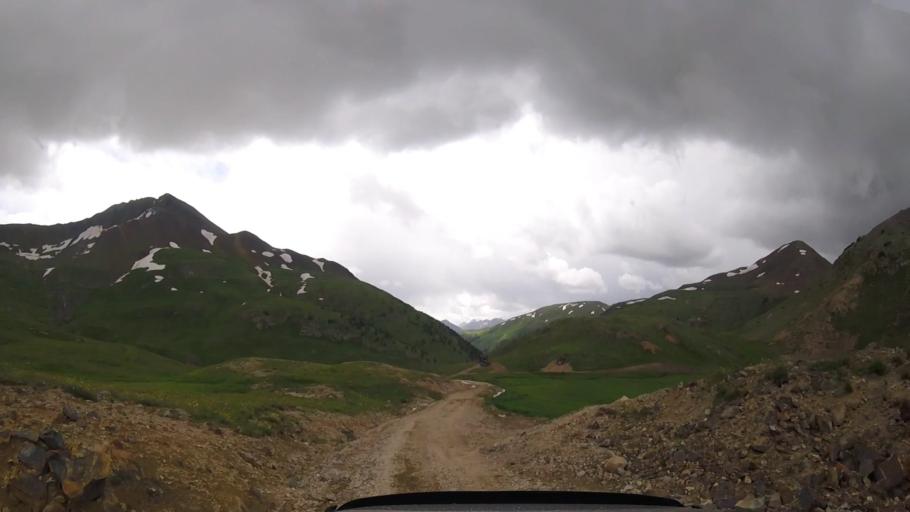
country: US
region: Colorado
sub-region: Ouray County
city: Ouray
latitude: 37.9534
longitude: -107.5747
